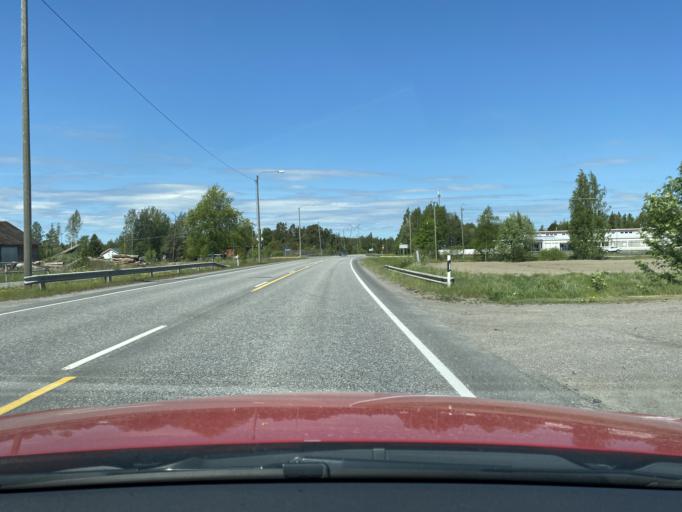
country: FI
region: Satakunta
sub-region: Rauma
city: Eura
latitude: 61.1228
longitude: 22.1321
